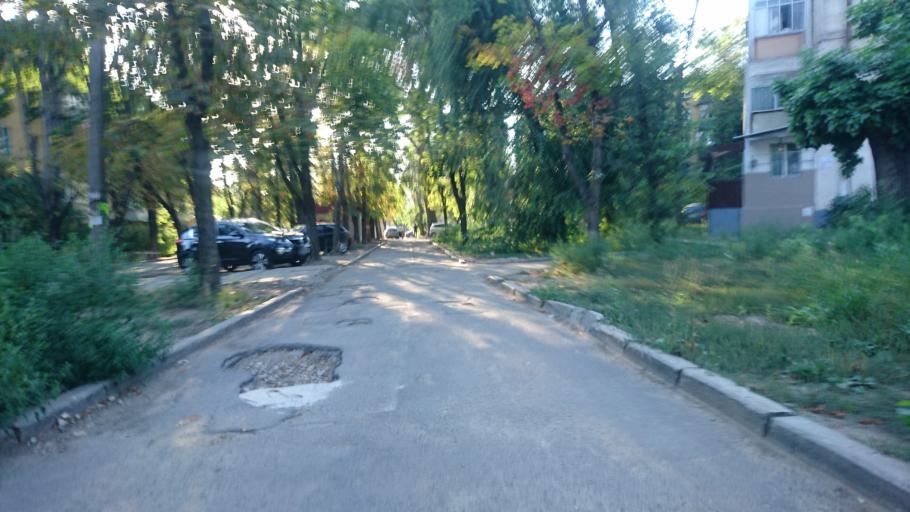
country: MD
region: Chisinau
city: Chisinau
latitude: 47.0397
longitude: 28.8610
